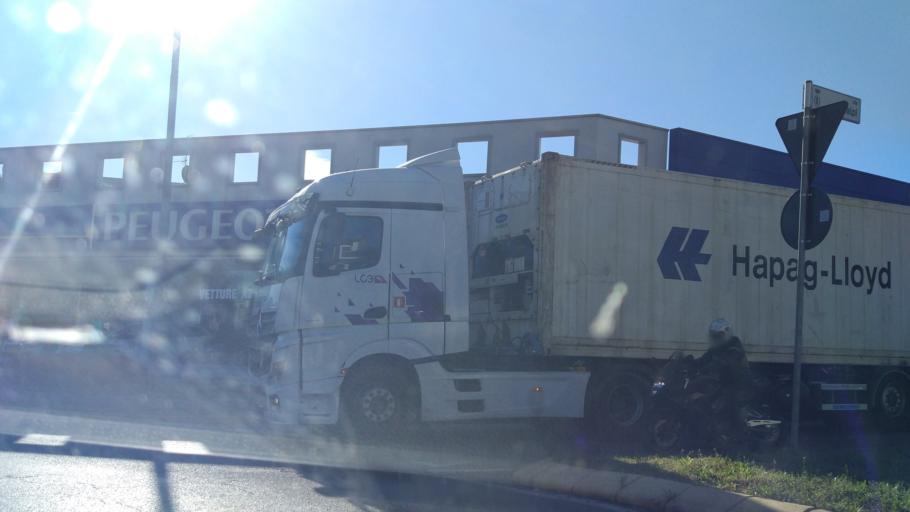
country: IT
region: Lombardy
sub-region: Provincia di Monza e Brianza
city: Giussano
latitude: 45.6963
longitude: 9.2147
